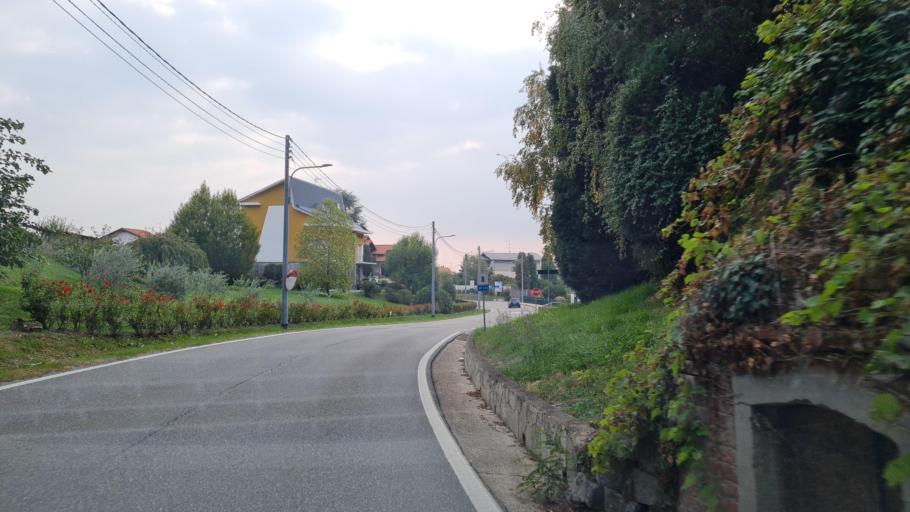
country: IT
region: Piedmont
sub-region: Provincia di Biella
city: Lessona
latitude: 45.5940
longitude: 8.1937
